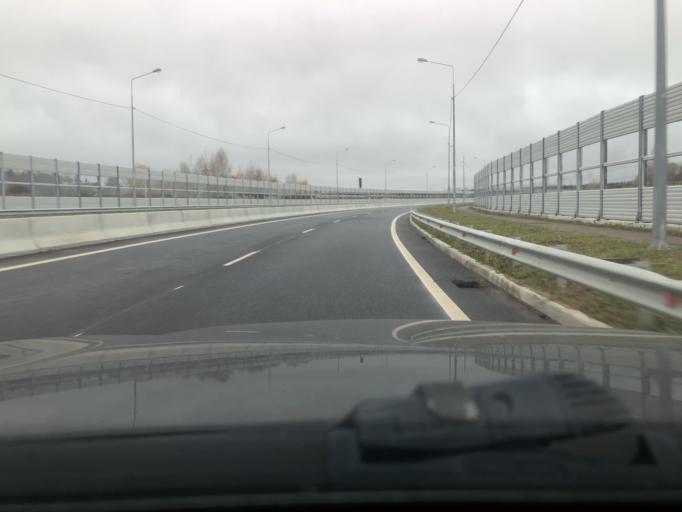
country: RU
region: Moskovskaya
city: Semkhoz
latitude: 56.3205
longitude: 38.0785
